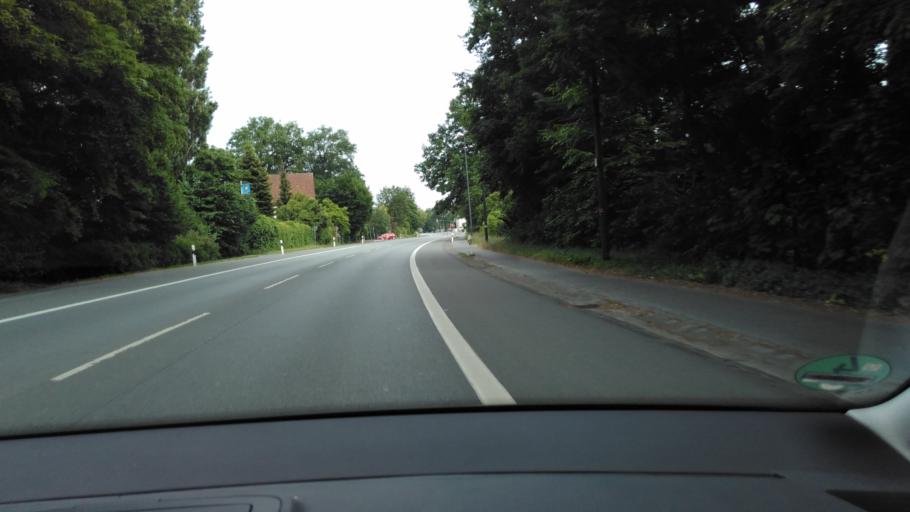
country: DE
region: North Rhine-Westphalia
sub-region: Regierungsbezirk Detmold
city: Guetersloh
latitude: 51.8957
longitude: 8.4076
